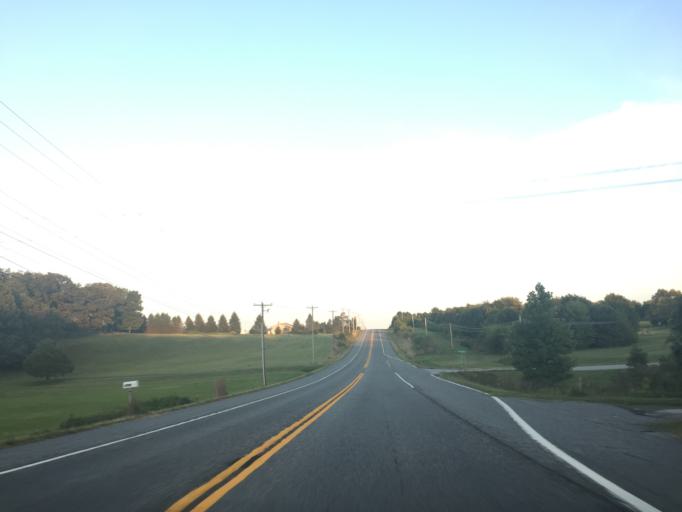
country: US
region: Pennsylvania
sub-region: York County
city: Susquehanna Trails
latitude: 39.6952
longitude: -76.3155
